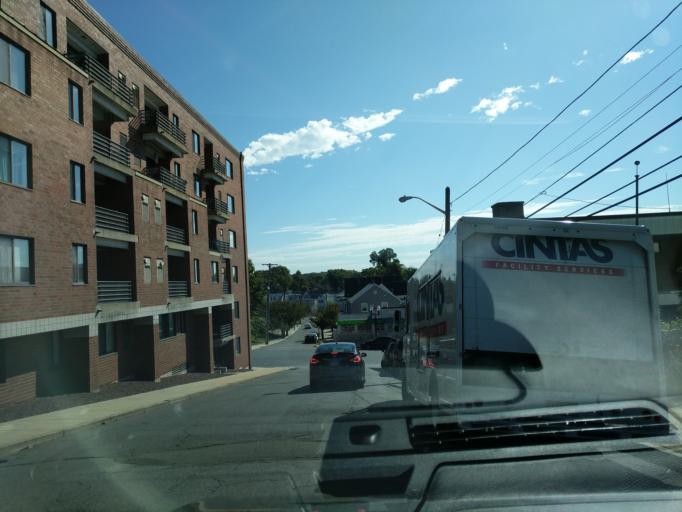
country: US
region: Massachusetts
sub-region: Suffolk County
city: Revere
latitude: 42.4072
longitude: -71.0149
